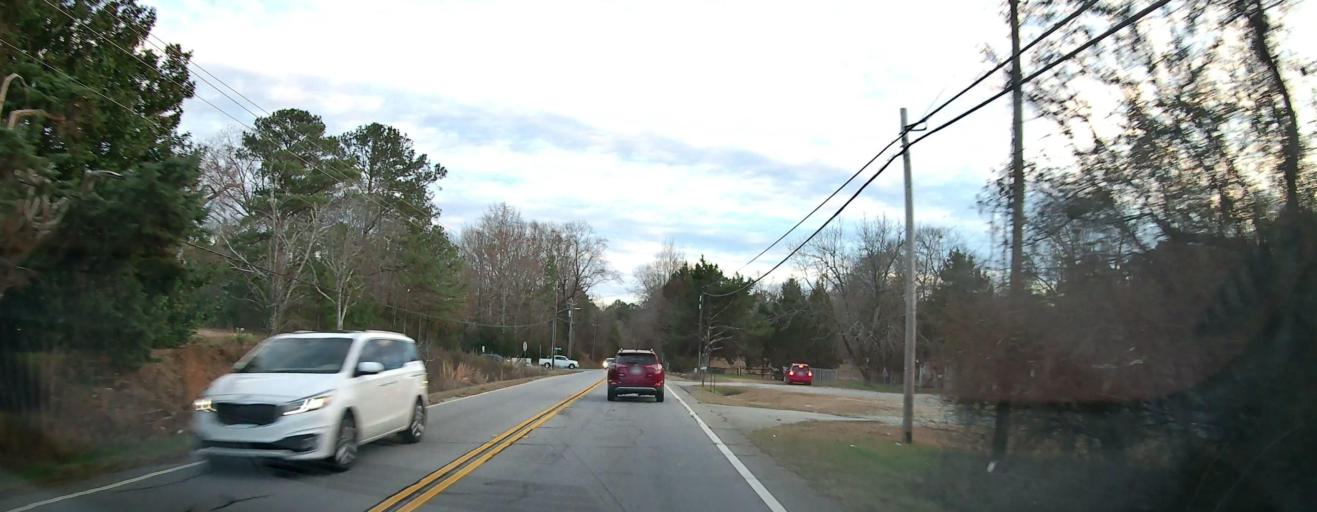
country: US
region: Alabama
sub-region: Russell County
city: Phenix City
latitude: 32.5839
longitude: -84.9113
